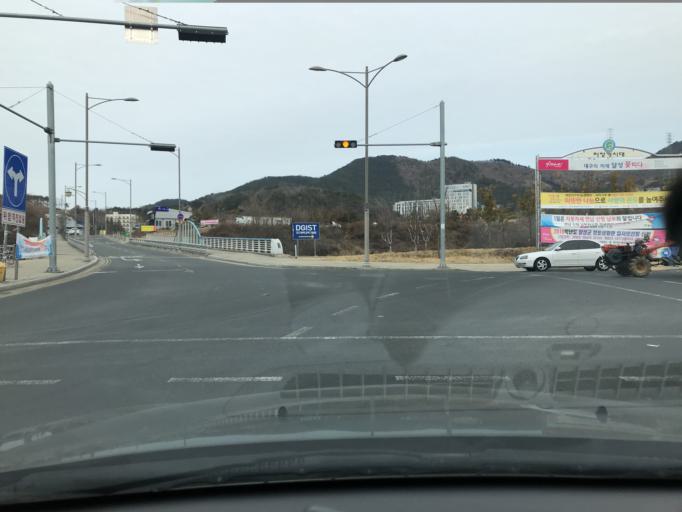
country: KR
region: Daegu
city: Hwawon
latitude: 35.6981
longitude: 128.4543
